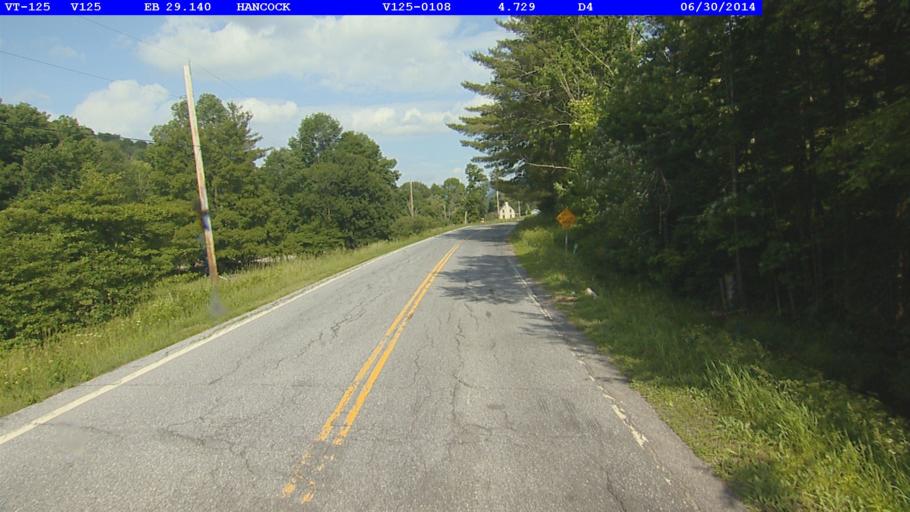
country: US
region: Vermont
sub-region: Orange County
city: Randolph
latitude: 43.9282
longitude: -72.8886
